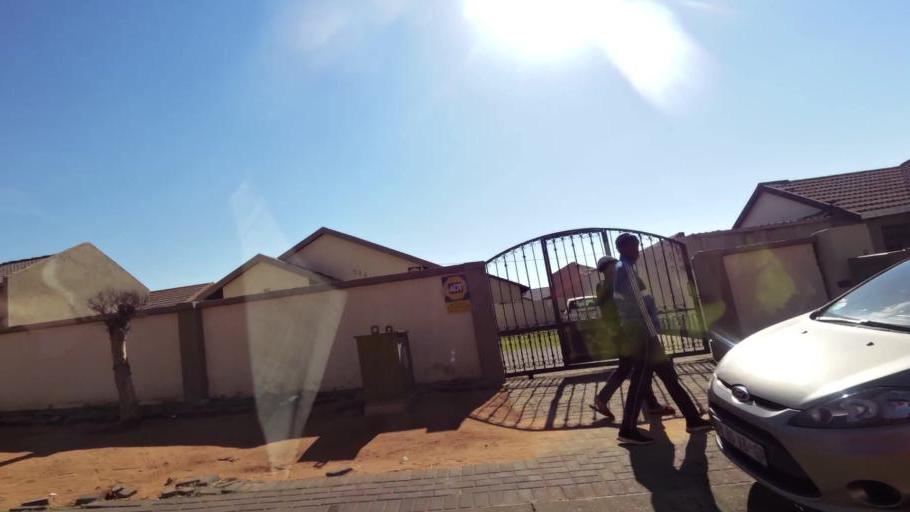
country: ZA
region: Gauteng
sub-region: City of Johannesburg Metropolitan Municipality
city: Johannesburg
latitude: -26.2495
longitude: 27.9830
